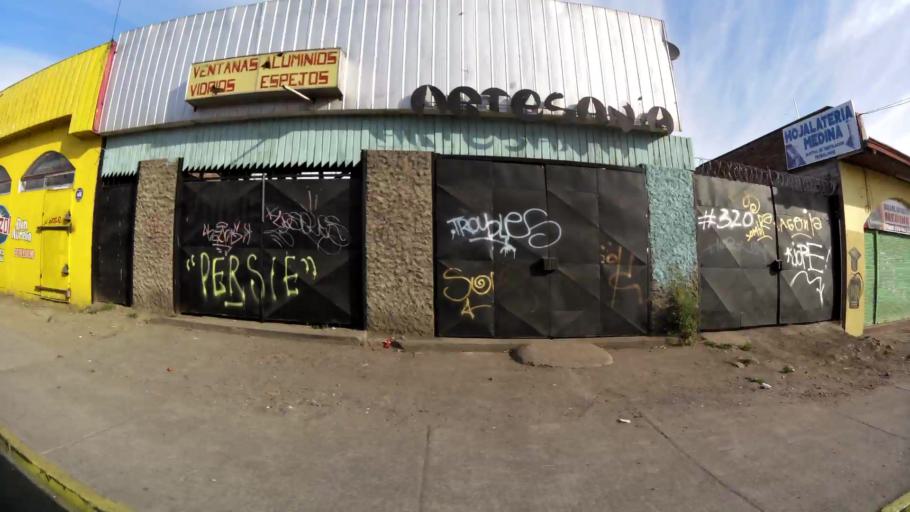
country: CL
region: Santiago Metropolitan
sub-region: Provincia de Cordillera
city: Puente Alto
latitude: -33.6128
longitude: -70.5802
